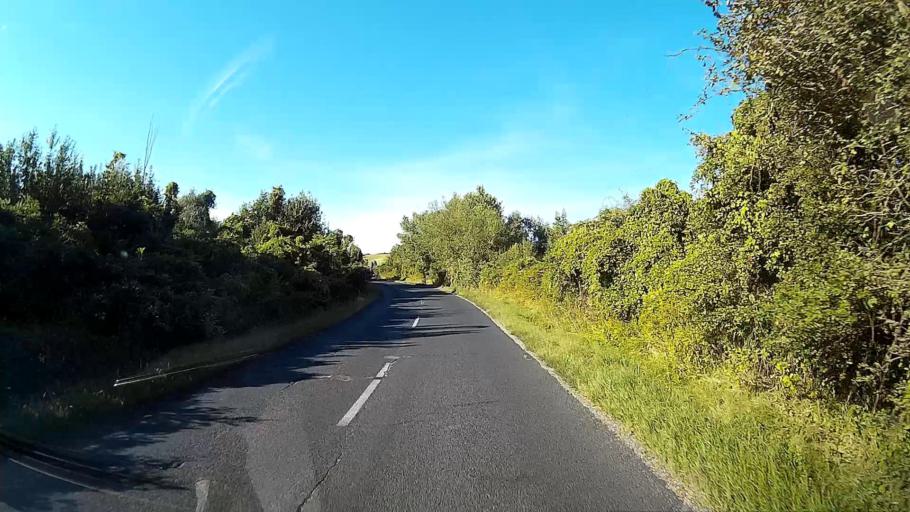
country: HU
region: Pest
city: Csobanka
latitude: 47.6316
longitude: 18.9549
